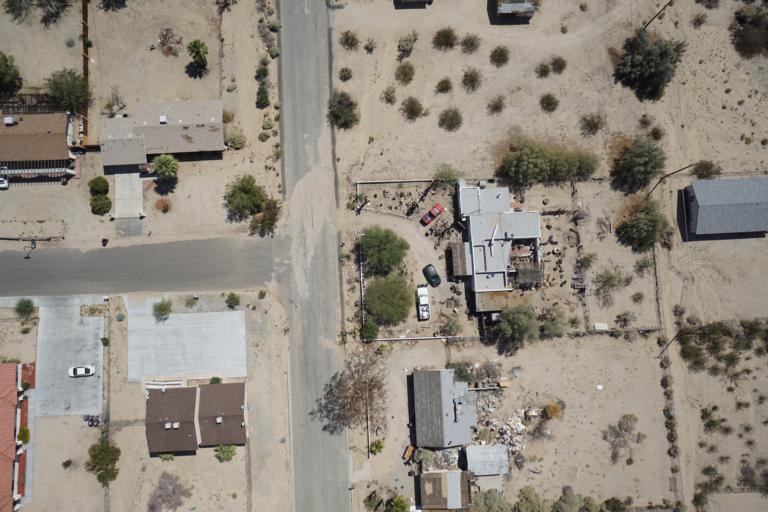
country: US
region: California
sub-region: San Bernardino County
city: Twentynine Palms
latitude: 34.1316
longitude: -116.0523
